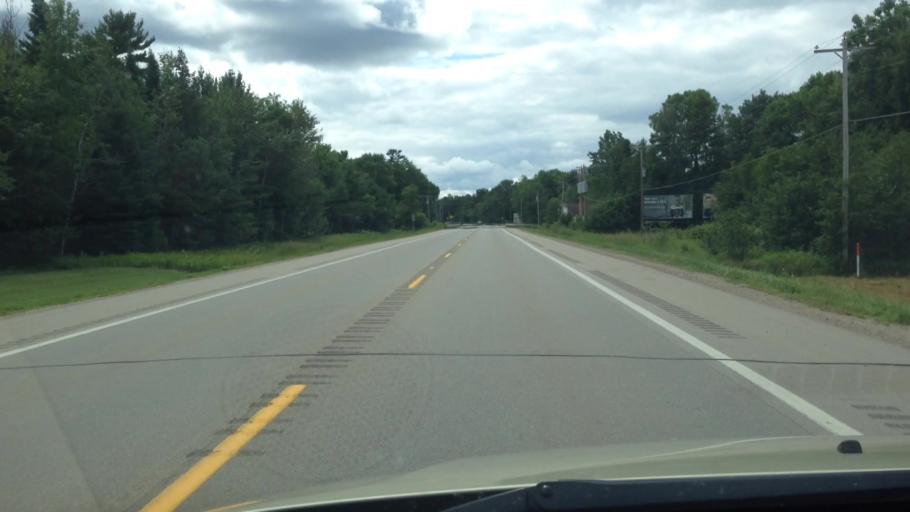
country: US
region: Michigan
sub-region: Menominee County
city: Menominee
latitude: 45.1834
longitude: -87.5649
